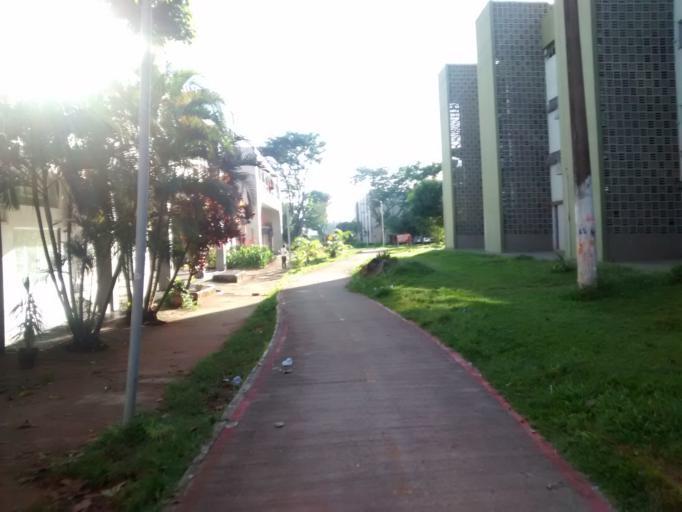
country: BR
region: Federal District
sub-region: Brasilia
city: Brasilia
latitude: -15.7542
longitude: -47.8822
